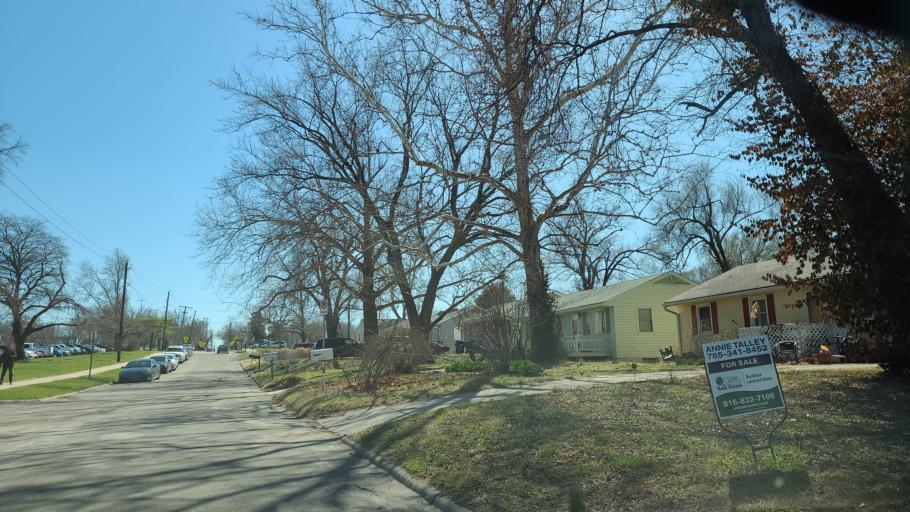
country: US
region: Kansas
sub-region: Douglas County
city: Lawrence
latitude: 38.9799
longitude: -95.2500
